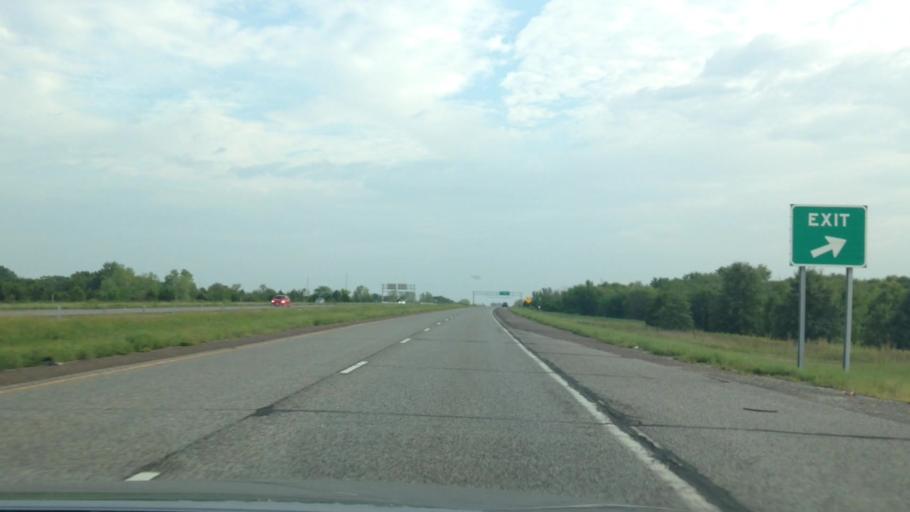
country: US
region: Missouri
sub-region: Clay County
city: Smithville
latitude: 39.3085
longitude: -94.5846
